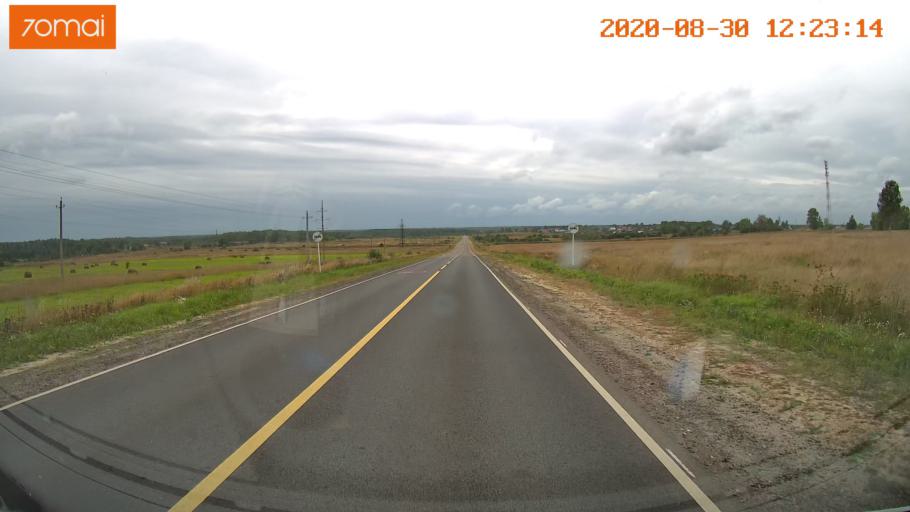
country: RU
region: Ivanovo
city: Yur'yevets
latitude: 57.3323
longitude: 42.8309
